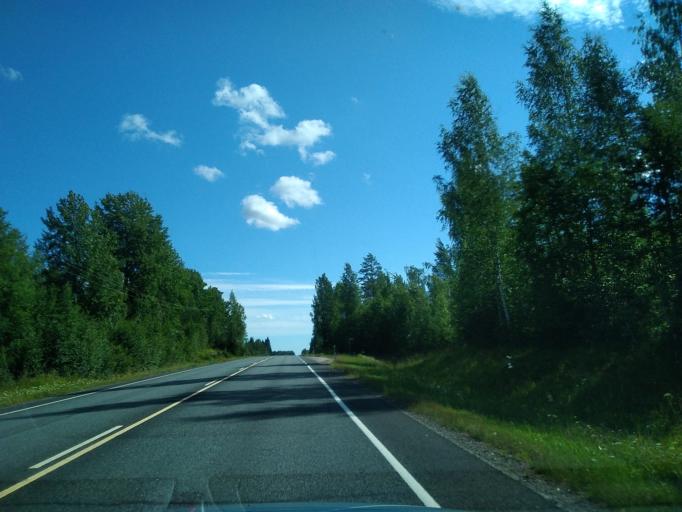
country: FI
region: Haeme
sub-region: Haemeenlinna
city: Renko
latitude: 60.8355
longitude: 24.0746
